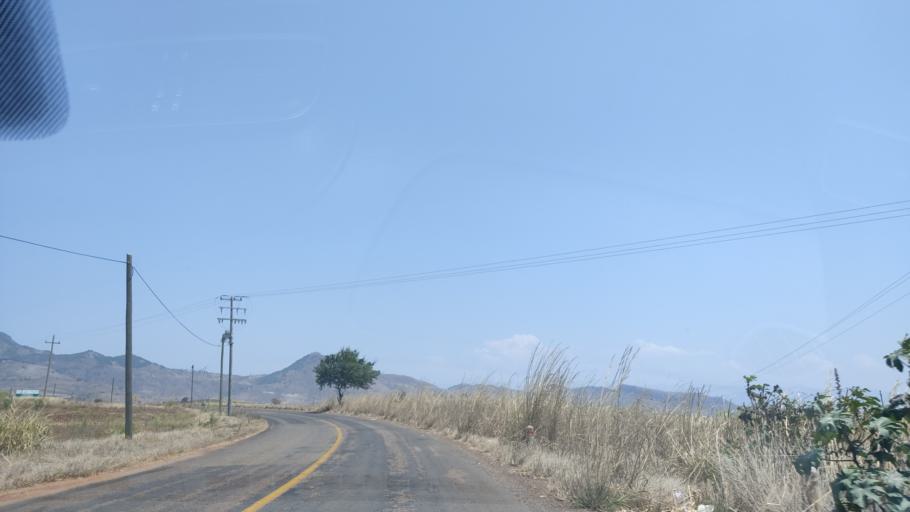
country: MX
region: Nayarit
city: Puga
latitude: 21.5892
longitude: -104.7425
